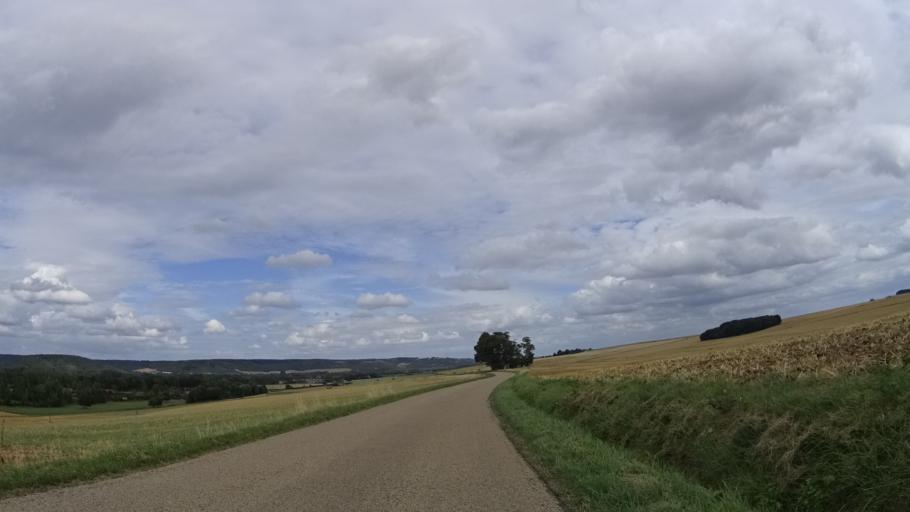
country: FR
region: Bourgogne
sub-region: Departement de l'Yonne
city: Cezy
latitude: 47.9820
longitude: 3.3038
